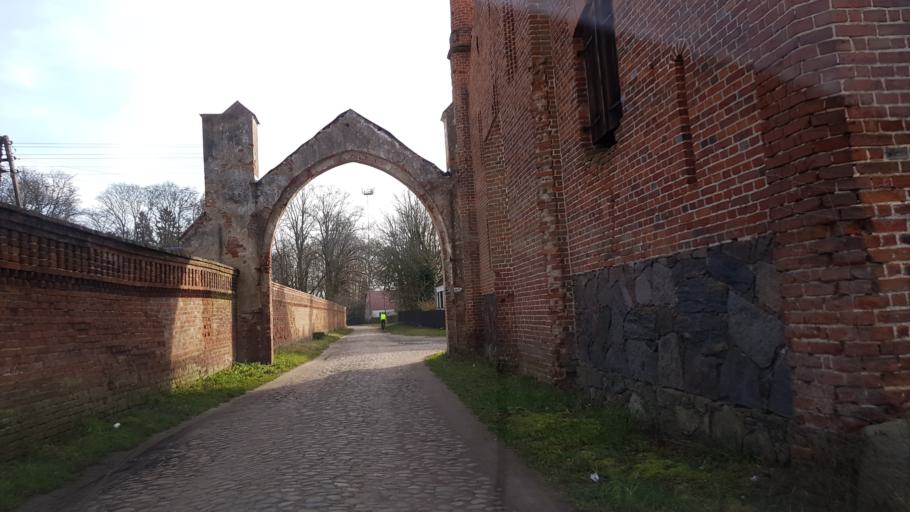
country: PL
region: West Pomeranian Voivodeship
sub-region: Powiat choszczenski
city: Pelczyce
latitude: 52.9399
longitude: 15.3584
